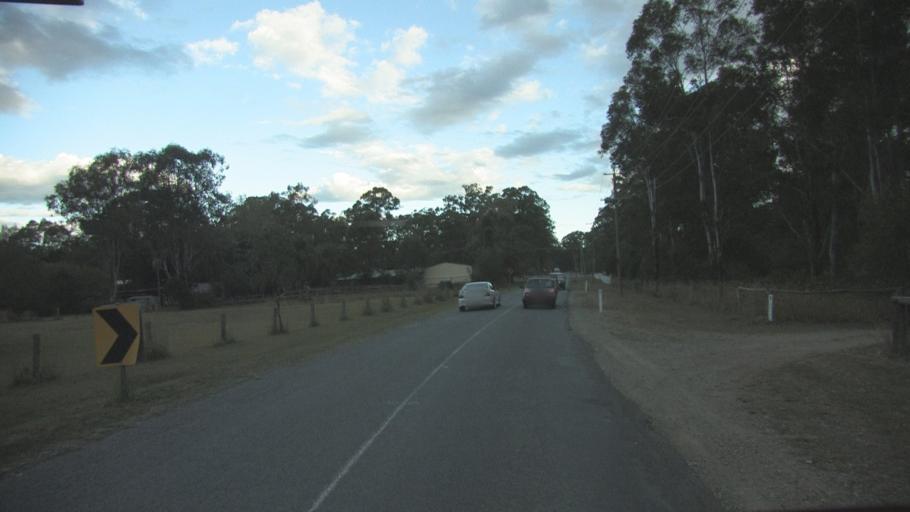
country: AU
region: Queensland
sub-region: Logan
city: Chambers Flat
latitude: -27.7857
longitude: 153.1357
